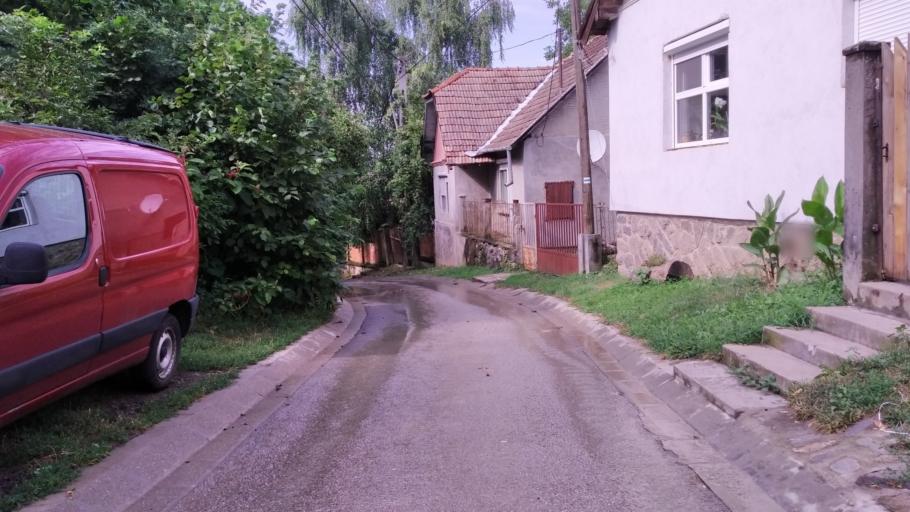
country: HU
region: Pest
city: Szob
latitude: 47.9343
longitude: 18.8257
